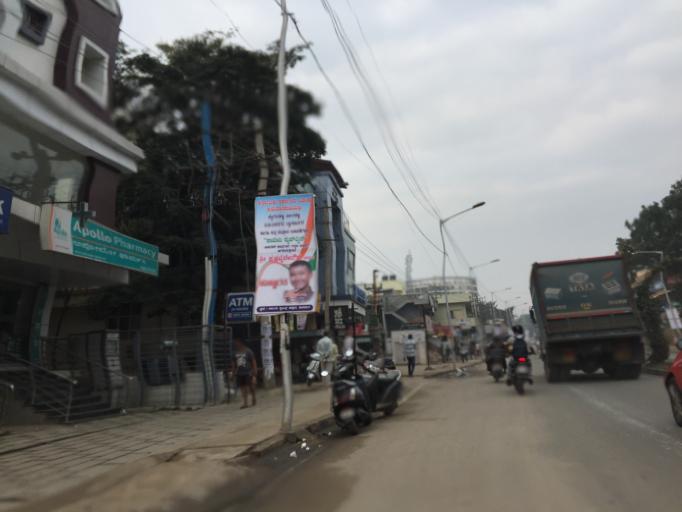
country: IN
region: Karnataka
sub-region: Bangalore Urban
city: Yelahanka
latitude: 13.1211
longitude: 77.6162
